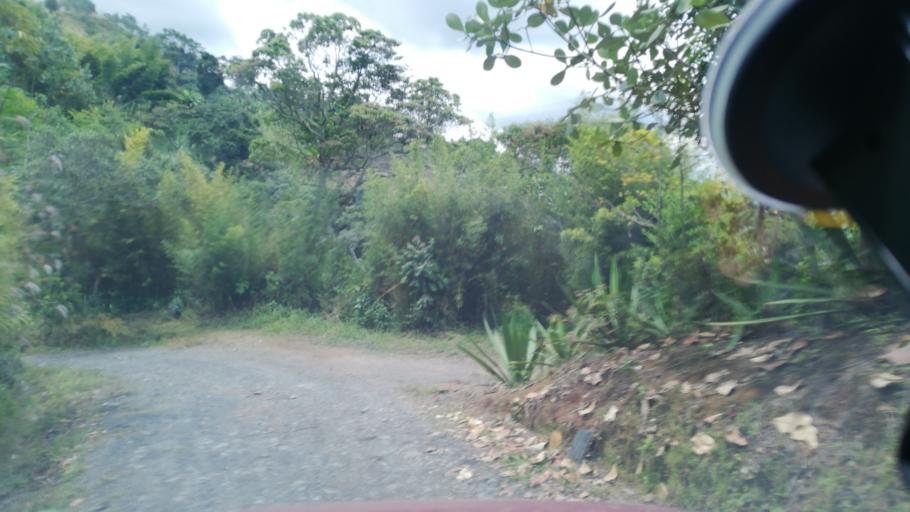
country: CO
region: Cundinamarca
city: Vergara
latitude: 5.1988
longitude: -74.2906
